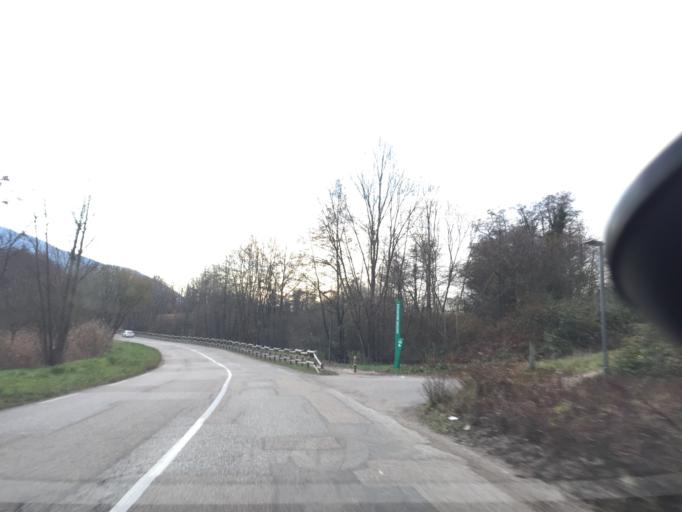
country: FR
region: Rhone-Alpes
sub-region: Departement de la Savoie
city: Drumettaz-Clarafond
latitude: 45.6541
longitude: 5.9137
